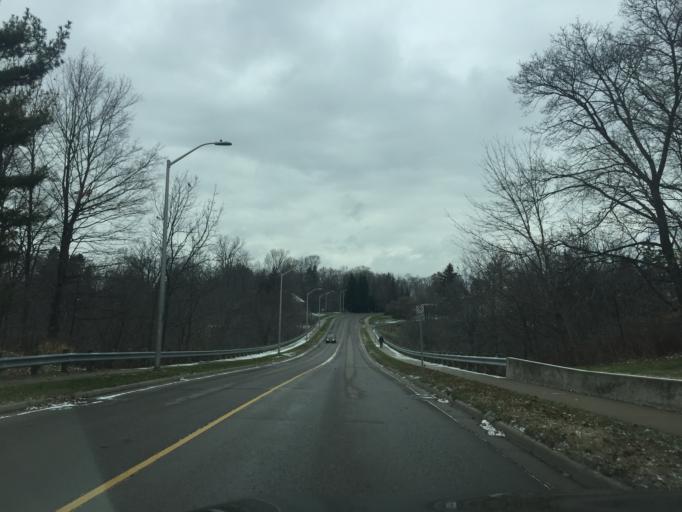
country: CA
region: Ontario
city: St. Thomas
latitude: 42.7712
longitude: -81.1969
